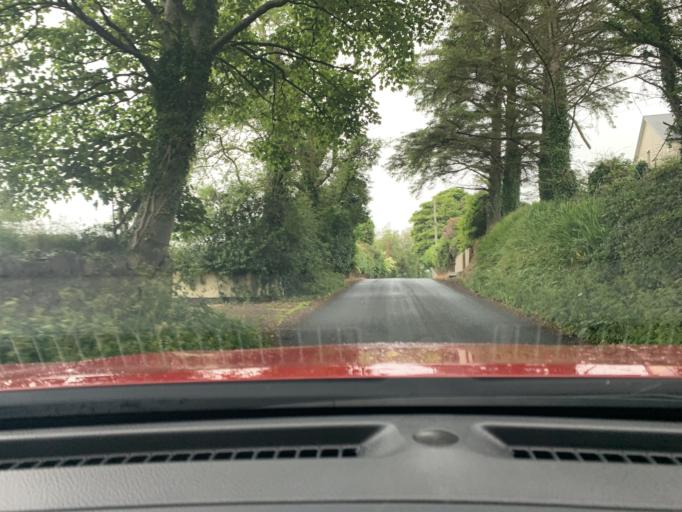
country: IE
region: Connaught
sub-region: Sligo
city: Sligo
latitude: 54.2933
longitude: -8.4634
